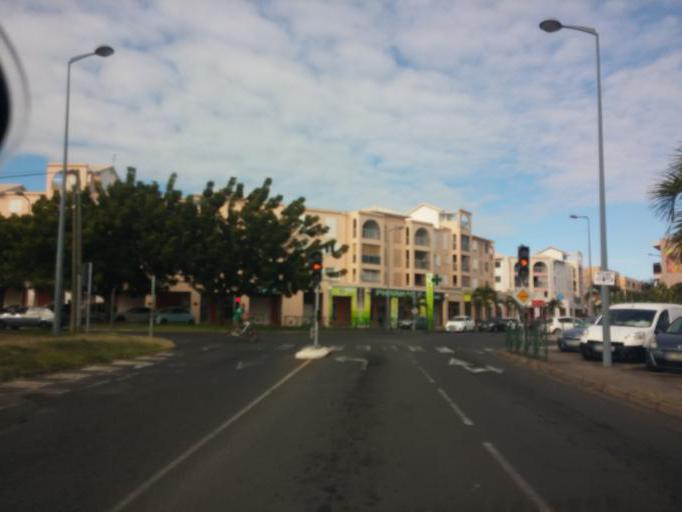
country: RE
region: Reunion
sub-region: Reunion
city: Le Port
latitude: -20.9383
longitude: 55.2966
